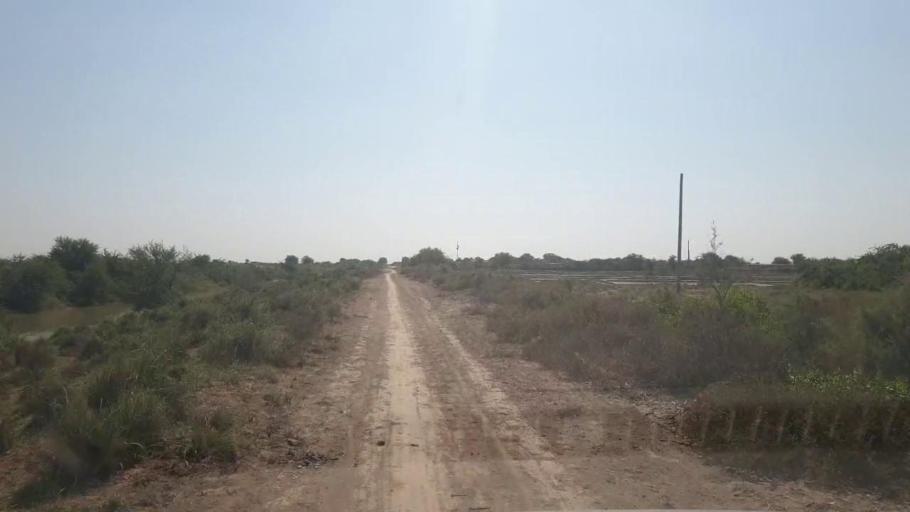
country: PK
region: Sindh
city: Tando Bago
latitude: 24.8929
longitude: 69.1645
